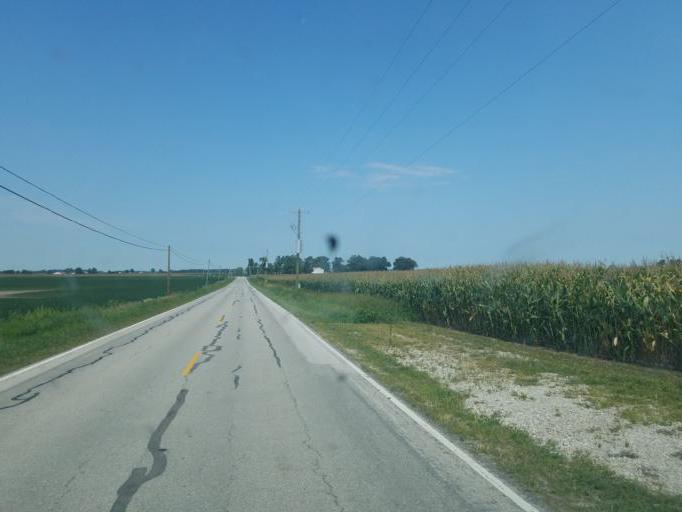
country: US
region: Ohio
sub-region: Marion County
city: Marion
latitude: 40.6459
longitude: -83.2195
